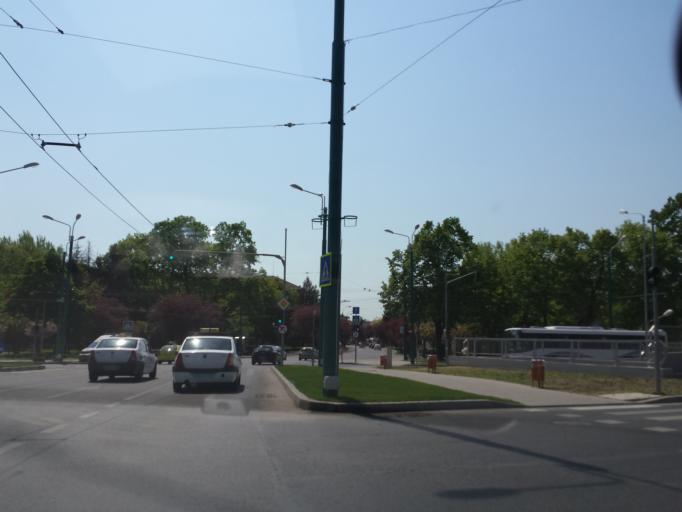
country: RO
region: Timis
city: Timisoara
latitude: 45.7490
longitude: 21.2353
